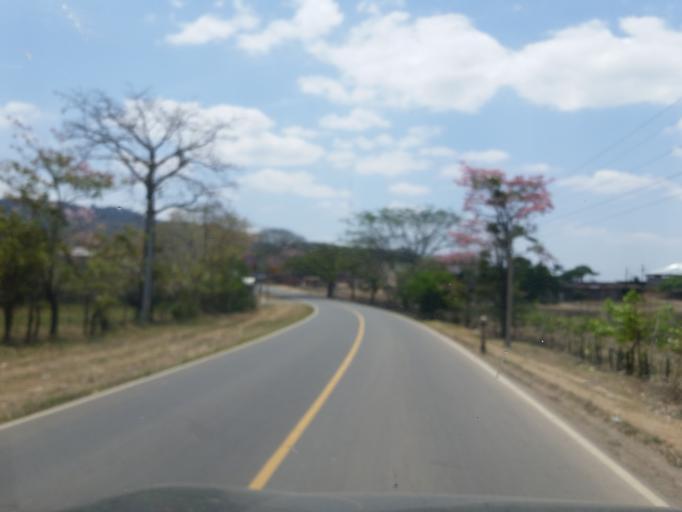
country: NI
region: Boaco
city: Boaco
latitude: 12.4829
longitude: -85.6442
